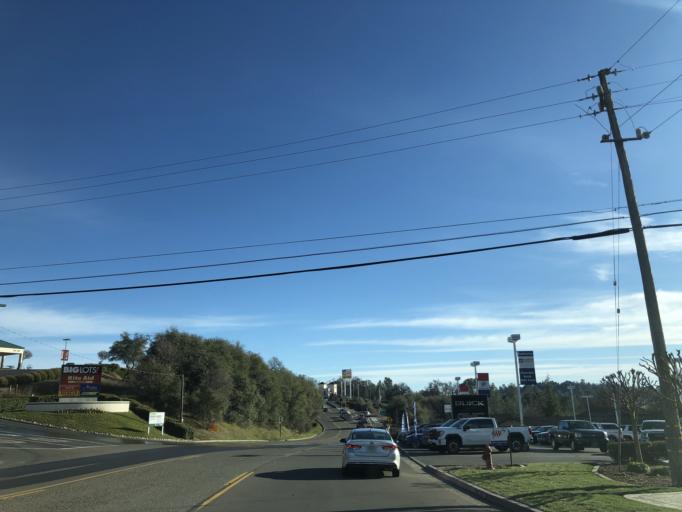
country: US
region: California
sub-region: El Dorado County
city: Diamond Springs
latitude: 38.7239
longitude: -120.8345
